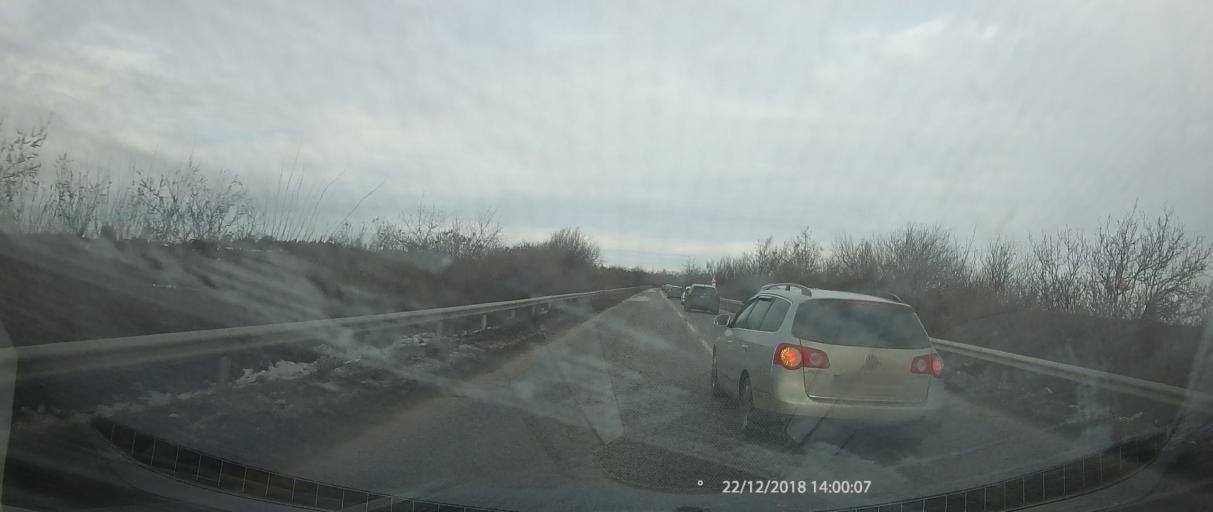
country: BG
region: Pleven
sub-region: Obshtina Dolni Dubnik
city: Dolni Dubnik
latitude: 43.3568
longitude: 24.3435
